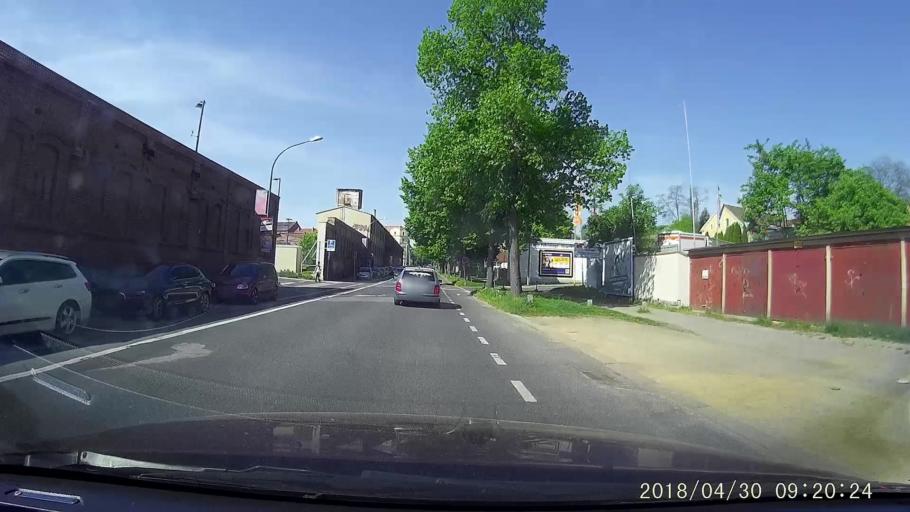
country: DE
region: Saxony
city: Goerlitz
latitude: 51.1551
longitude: 14.9792
